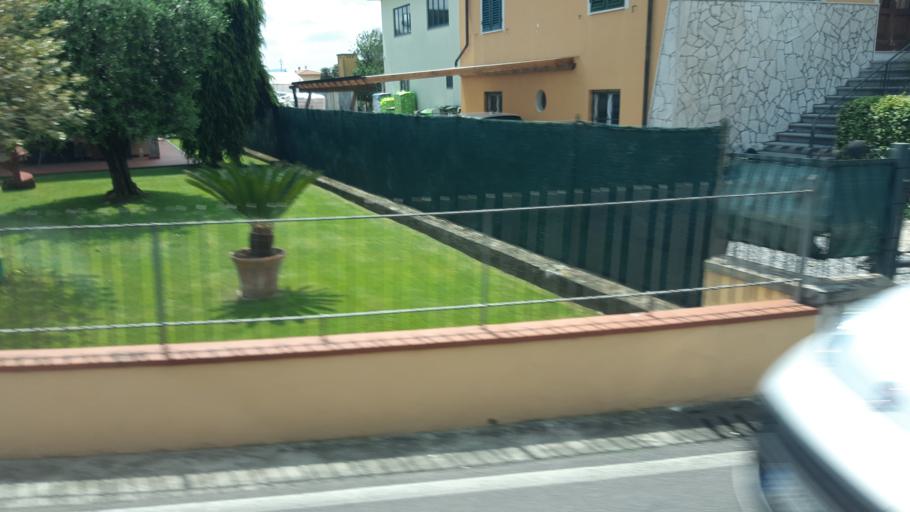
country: IT
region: Tuscany
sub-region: Provincia di Lucca
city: Capannori
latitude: 43.8684
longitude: 10.5393
